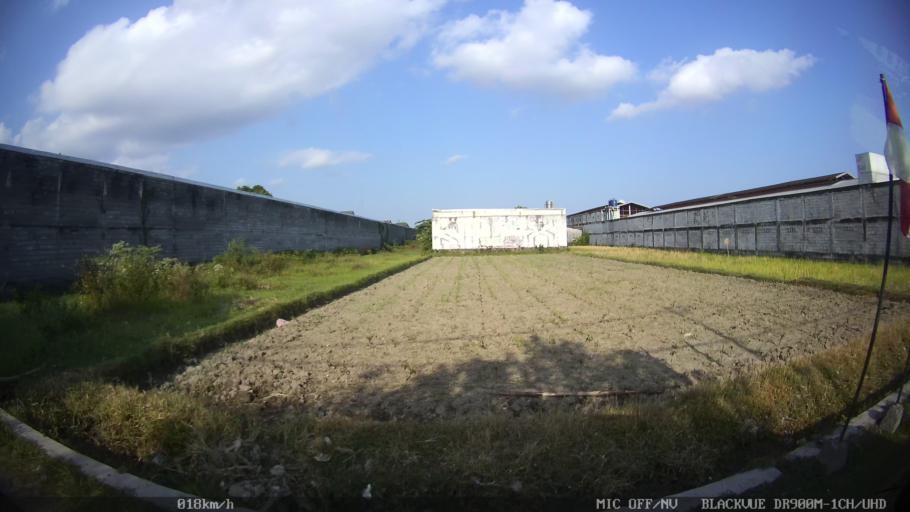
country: ID
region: Daerah Istimewa Yogyakarta
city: Yogyakarta
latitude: -7.7820
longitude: 110.3484
